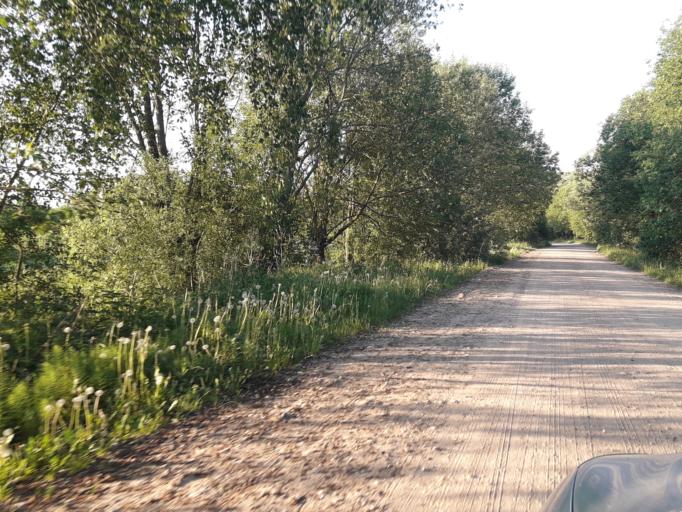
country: BY
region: Minsk
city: Pyatryshki
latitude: 54.1326
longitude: 27.1413
